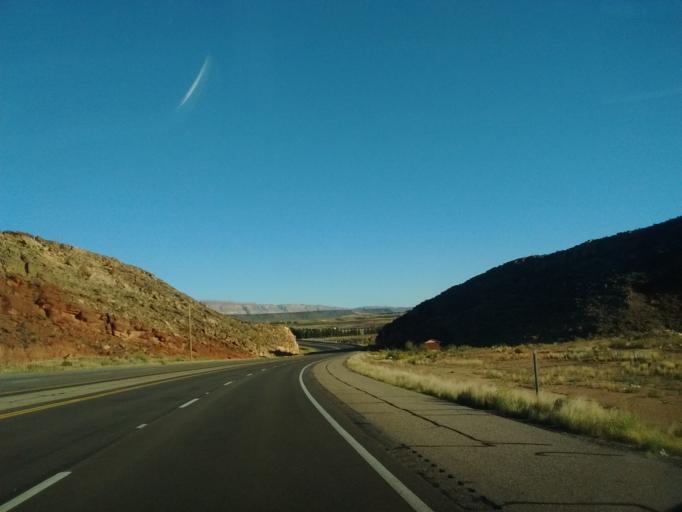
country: US
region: Utah
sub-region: Washington County
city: Hurricane
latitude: 37.1666
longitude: -113.3989
